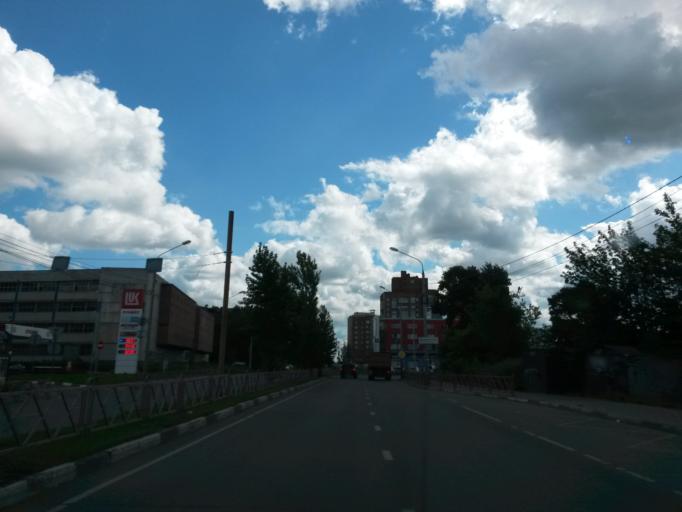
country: RU
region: Jaroslavl
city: Yaroslavl
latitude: 57.6184
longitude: 39.8545
